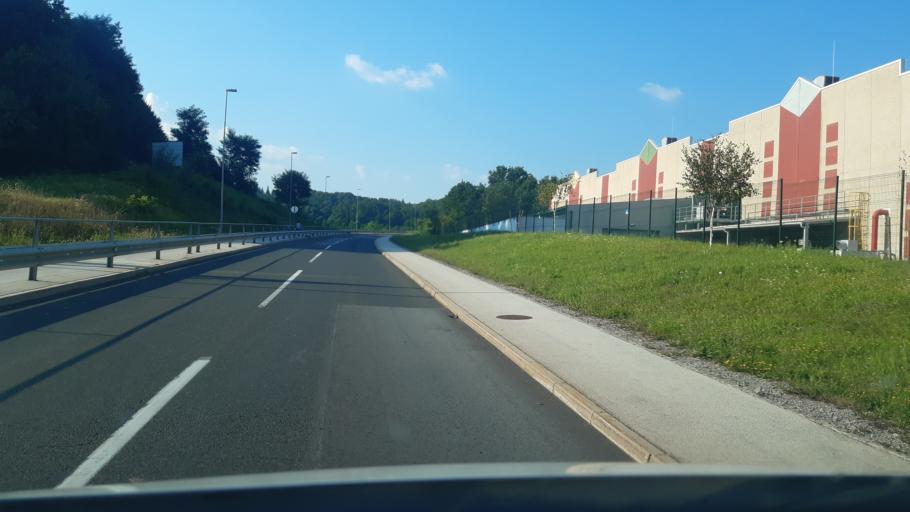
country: SI
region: Crnomelj
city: Crnomelj
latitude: 45.5733
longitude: 15.1805
